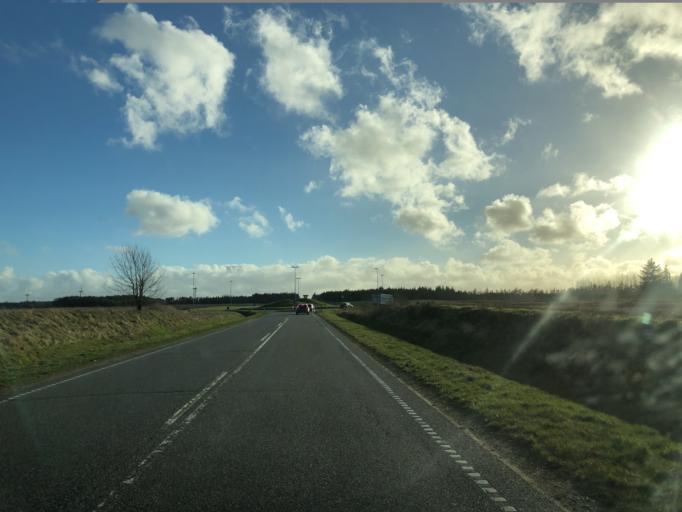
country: DK
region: Central Jutland
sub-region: Herning Kommune
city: Vildbjerg
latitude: 56.1842
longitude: 8.7033
